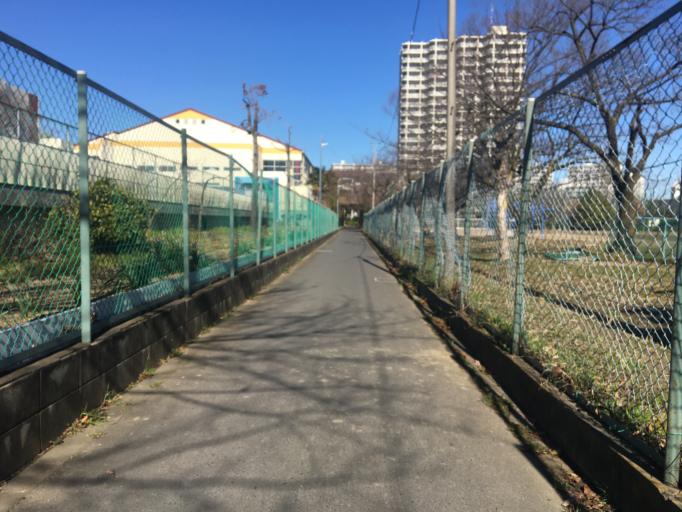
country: JP
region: Saitama
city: Shiki
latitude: 35.8262
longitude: 139.5617
